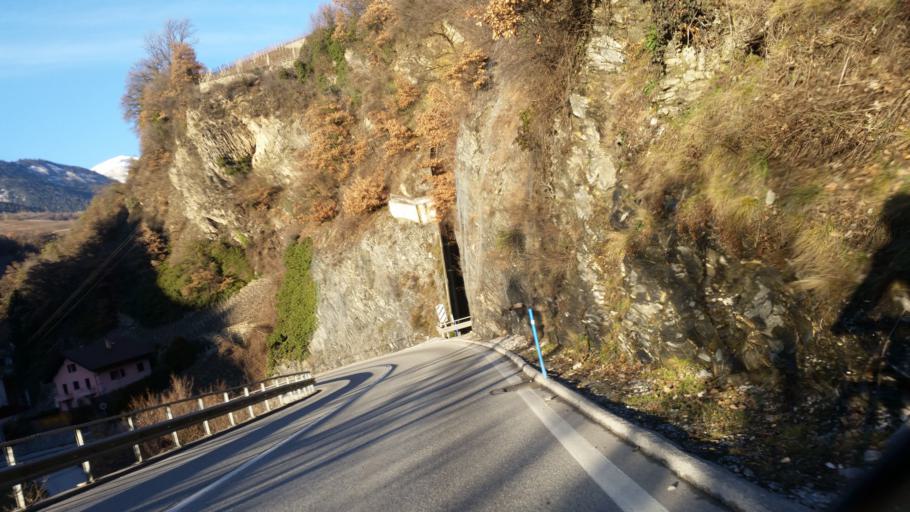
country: CH
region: Valais
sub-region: Sion District
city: Sitten
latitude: 46.2447
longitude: 7.3641
